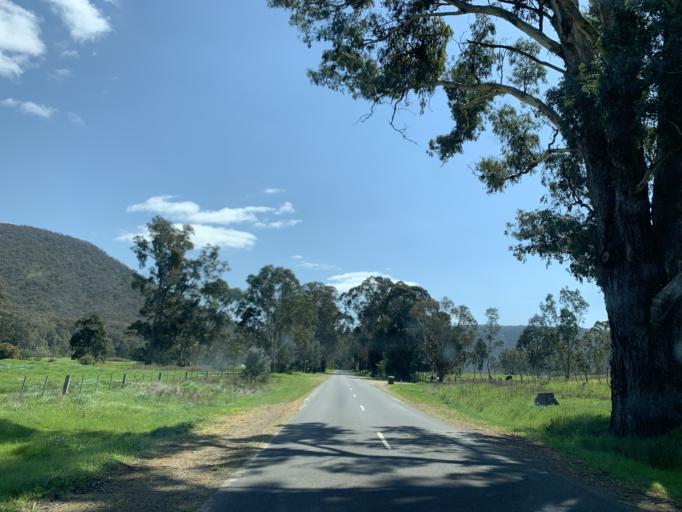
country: AU
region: Victoria
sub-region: Mansfield
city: Mansfield
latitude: -36.7831
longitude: 146.1386
